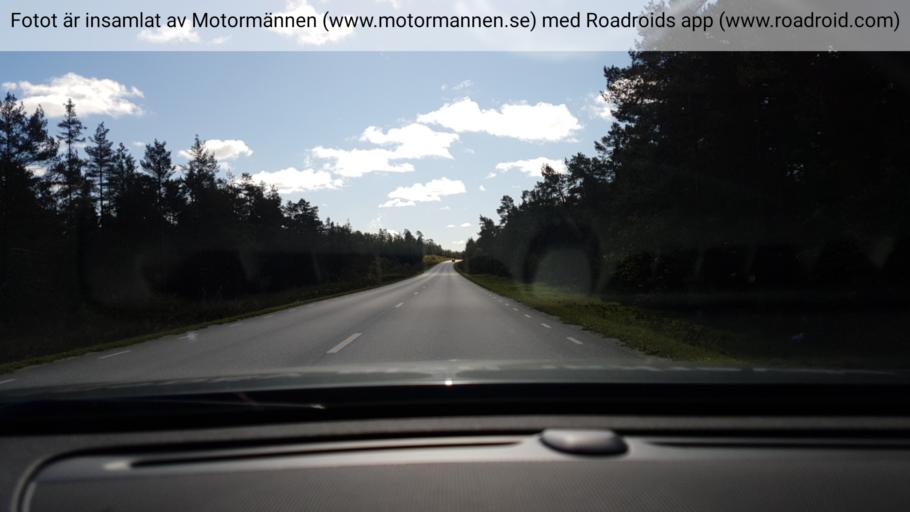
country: SE
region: Gotland
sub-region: Gotland
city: Slite
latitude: 57.7426
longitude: 18.7897
